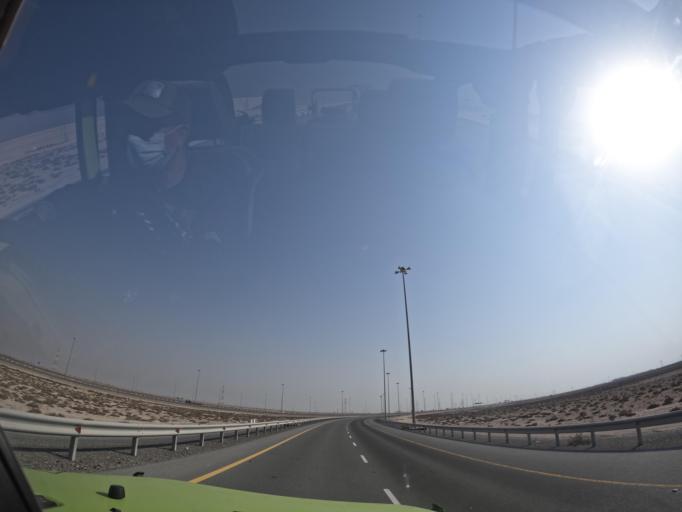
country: AE
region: Abu Dhabi
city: Abu Dhabi
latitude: 24.6751
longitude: 54.8119
